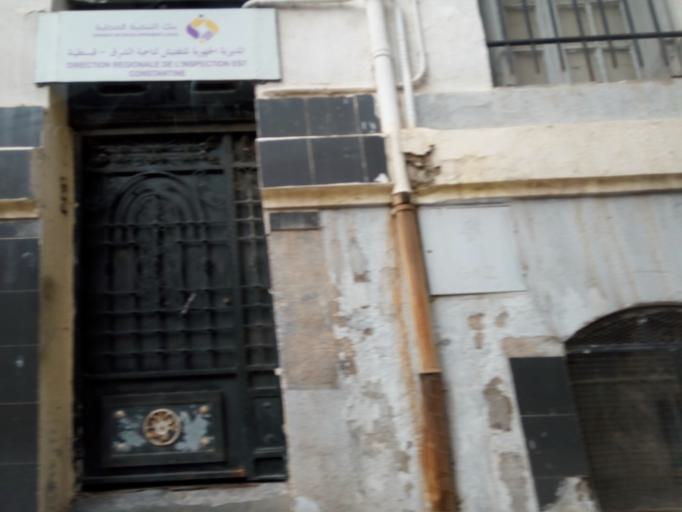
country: DZ
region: Constantine
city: Constantine
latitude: 36.3693
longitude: 6.6166
